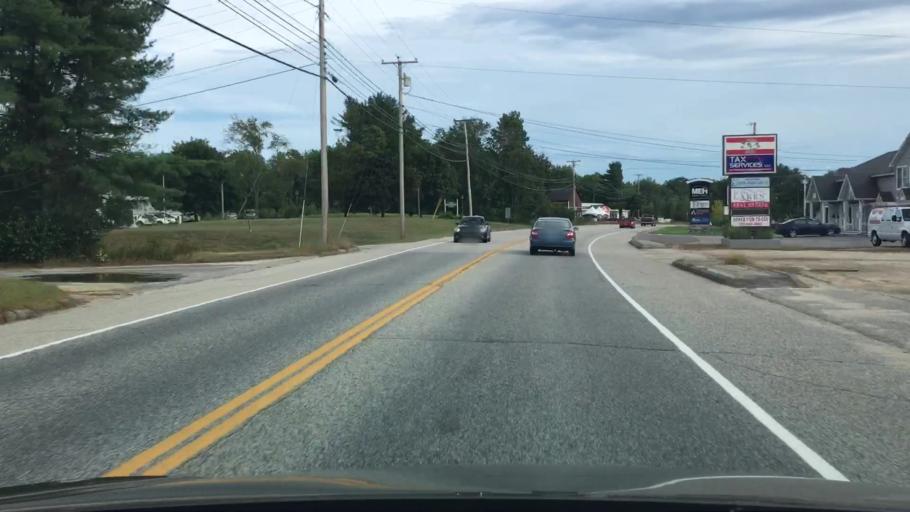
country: US
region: Maine
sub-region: Cumberland County
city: Bridgton
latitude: 44.0426
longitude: -70.7002
